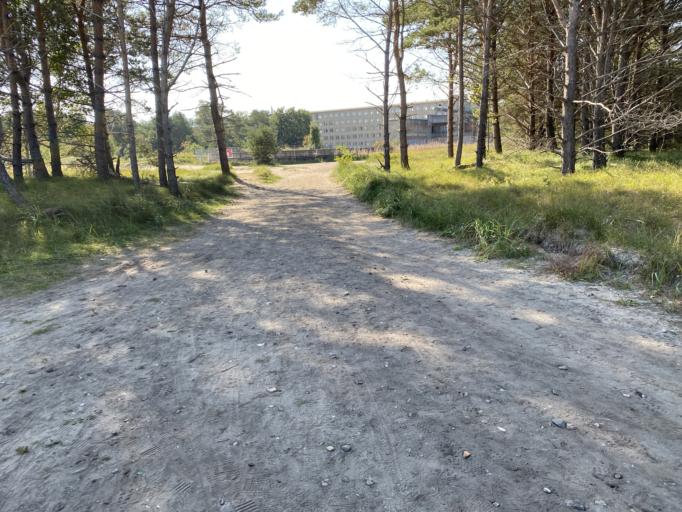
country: DE
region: Mecklenburg-Vorpommern
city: Ostseebad Binz
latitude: 54.4403
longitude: 13.5777
